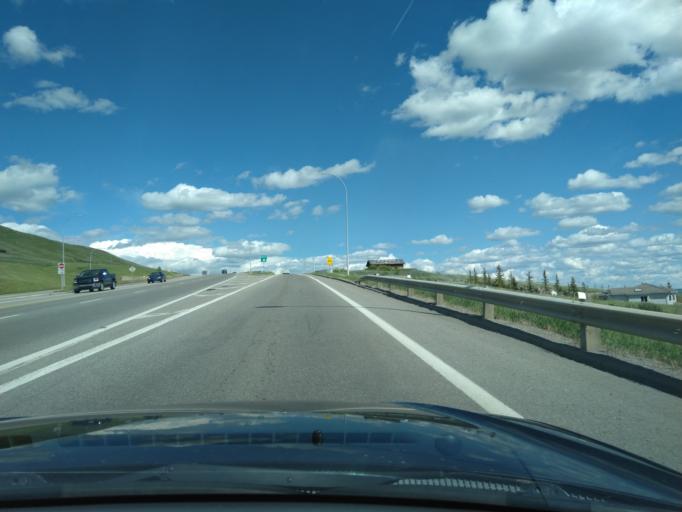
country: CA
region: Alberta
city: Cochrane
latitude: 51.1911
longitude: -114.4555
